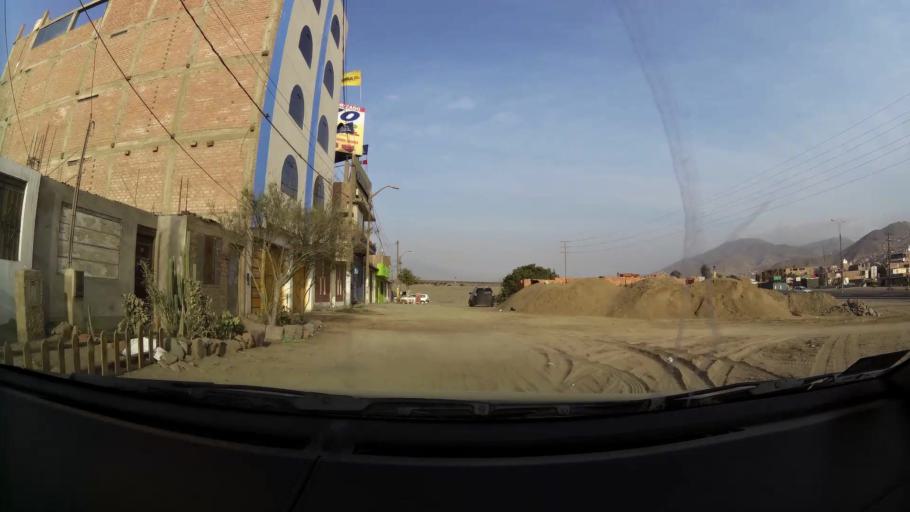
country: PE
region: Lima
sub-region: Lima
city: Santa Rosa
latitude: -11.7762
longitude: -77.1626
